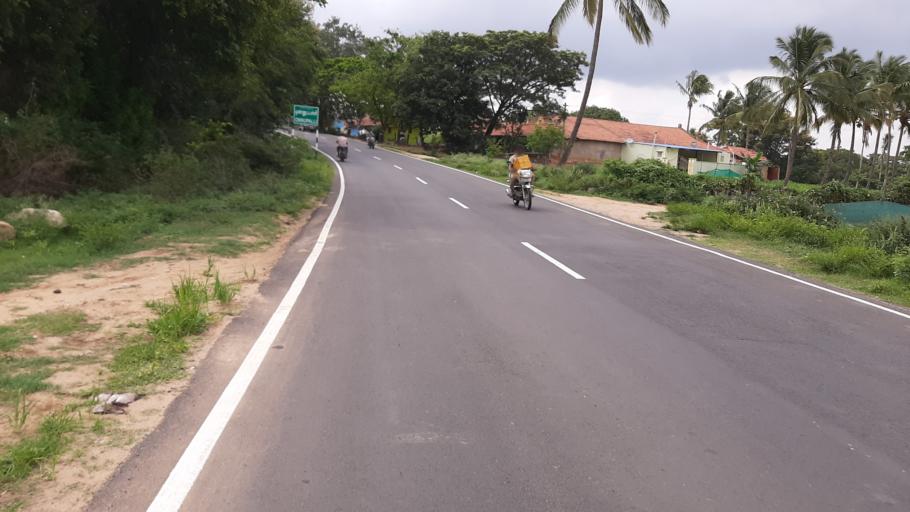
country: IN
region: Tamil Nadu
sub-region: Krishnagiri
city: Denkanikota
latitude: 12.5364
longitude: 77.7727
